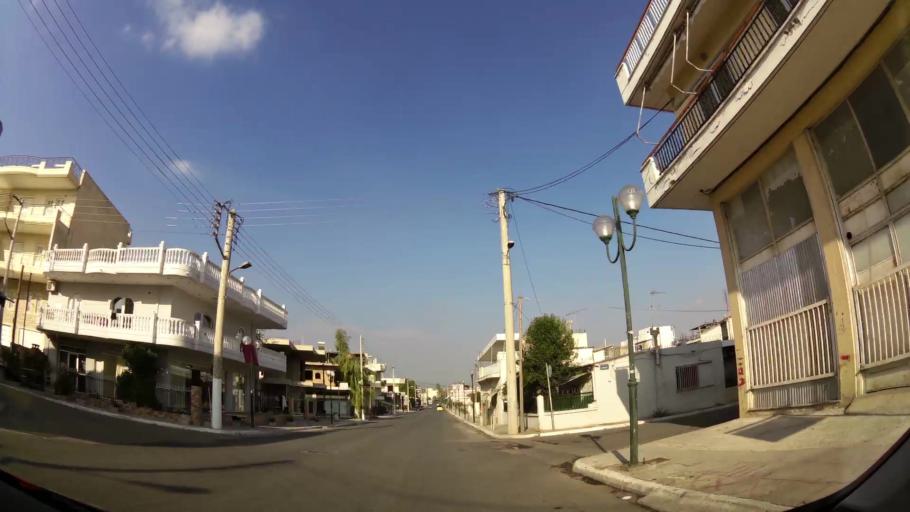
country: GR
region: Attica
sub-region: Nomarchia Dytikis Attikis
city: Zefyri
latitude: 38.0725
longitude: 23.7180
